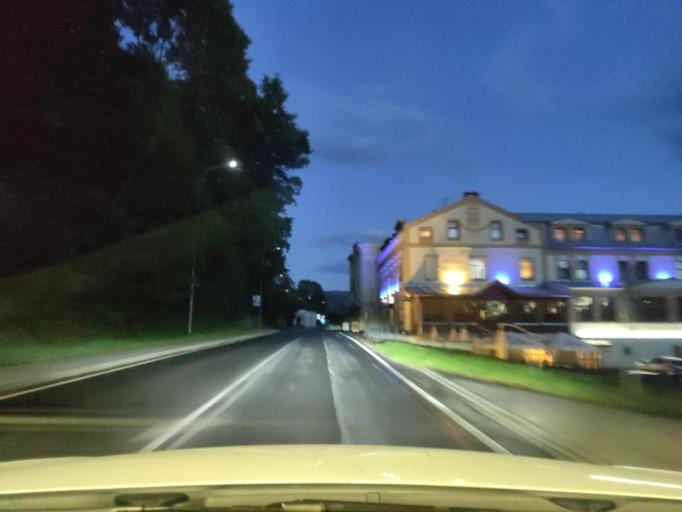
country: CZ
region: Olomoucky
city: Zlate Hory
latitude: 50.2594
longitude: 17.3989
